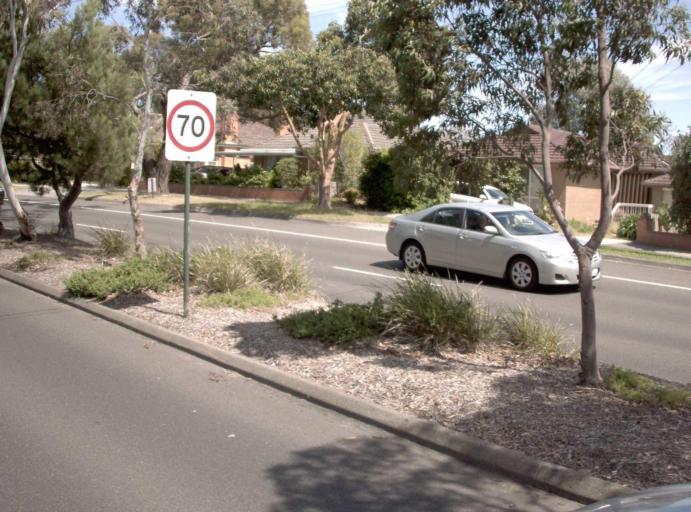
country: AU
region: Victoria
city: Burwood East
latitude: -37.8464
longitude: 145.1536
